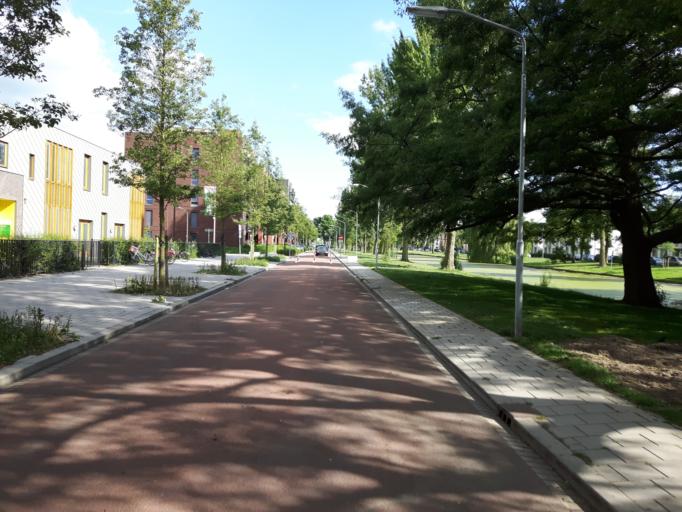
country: NL
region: South Holland
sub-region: Gemeente Dordrecht
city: Dordrecht
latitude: 51.8031
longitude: 4.6704
